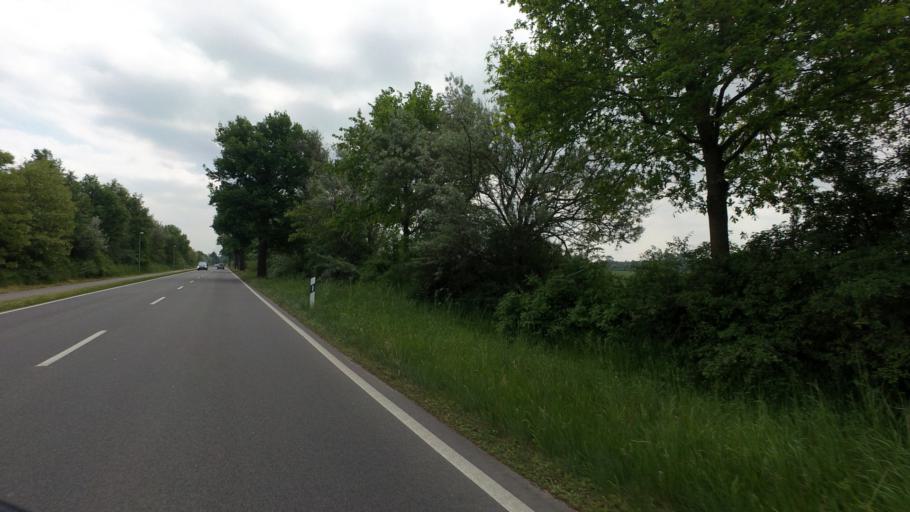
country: DE
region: Brandenburg
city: Drehnow
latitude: 51.8663
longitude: 14.3889
